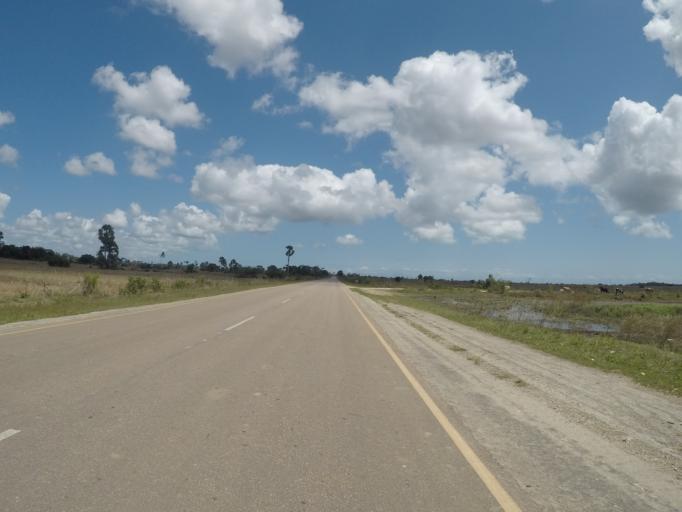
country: TZ
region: Zanzibar Central/South
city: Koani
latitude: -6.1889
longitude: 39.3712
